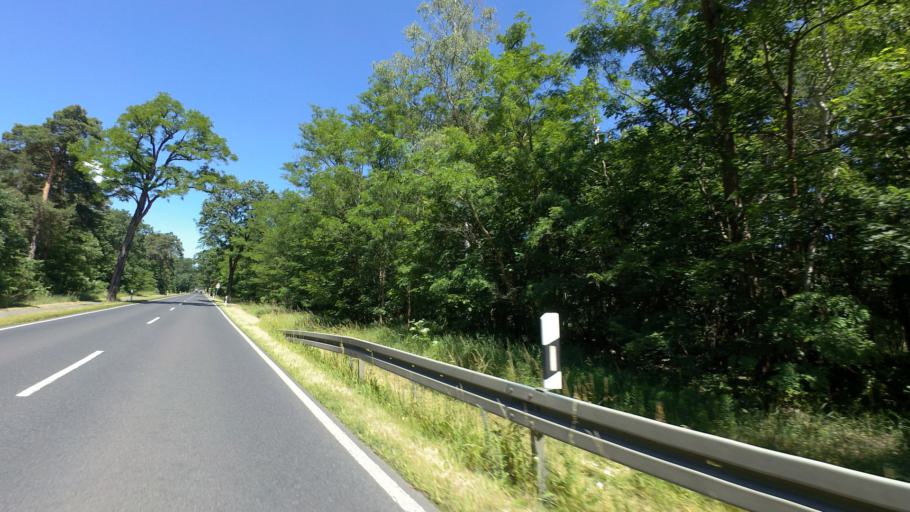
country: DE
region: Brandenburg
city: Baruth
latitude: 52.0747
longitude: 13.5036
